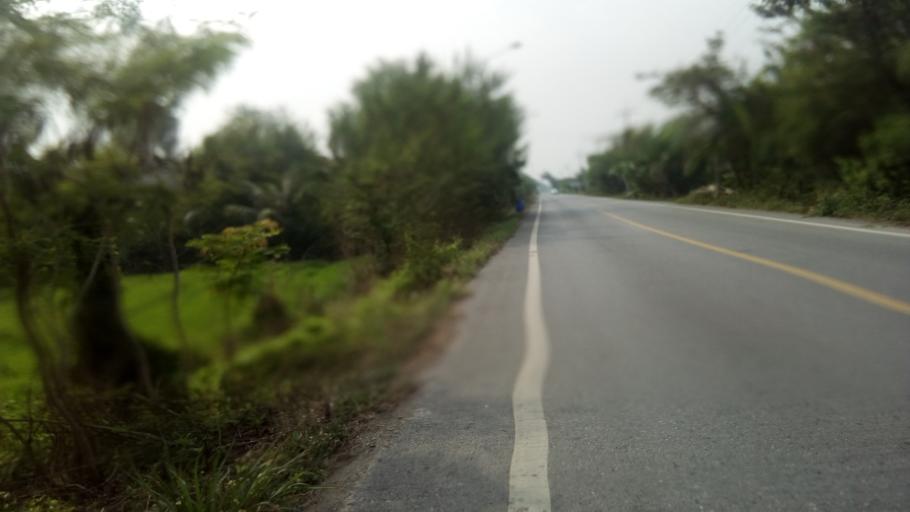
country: TH
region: Pathum Thani
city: Ban Rangsit
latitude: 14.0334
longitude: 100.8246
